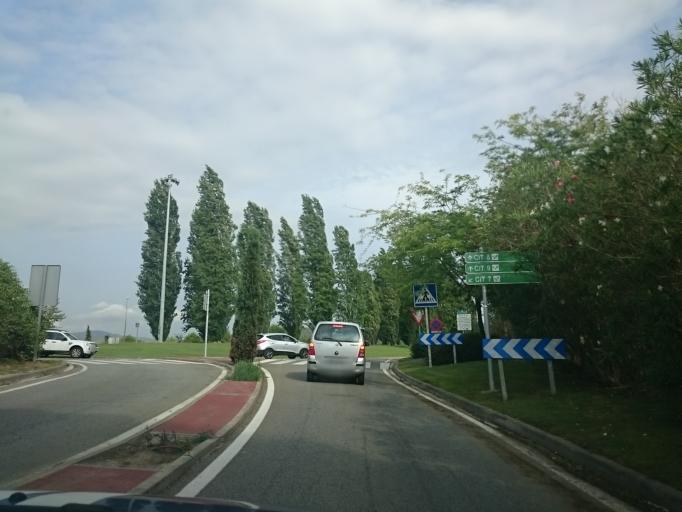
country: ES
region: Catalonia
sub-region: Provincia de Barcelona
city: Sant Cugat del Valles
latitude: 41.4815
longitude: 2.0912
